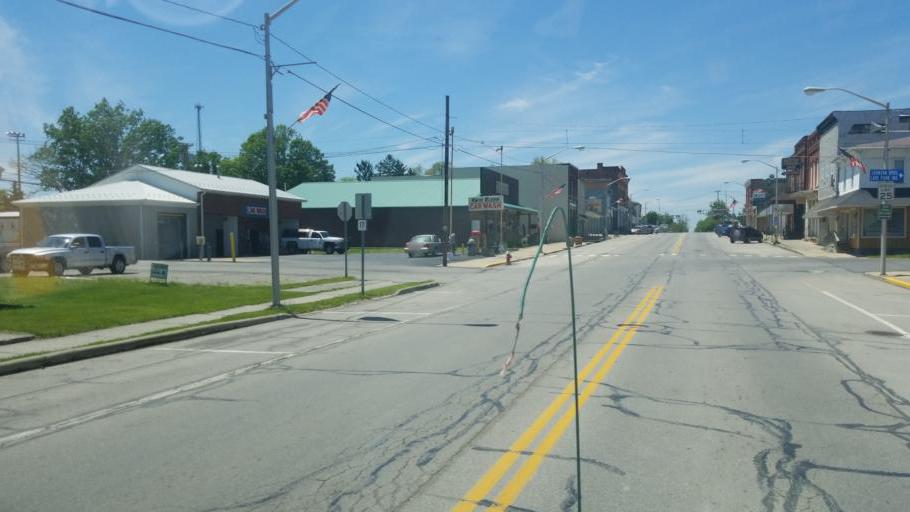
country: US
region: Ohio
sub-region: Huron County
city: Greenwich
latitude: 41.0299
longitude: -82.5161
